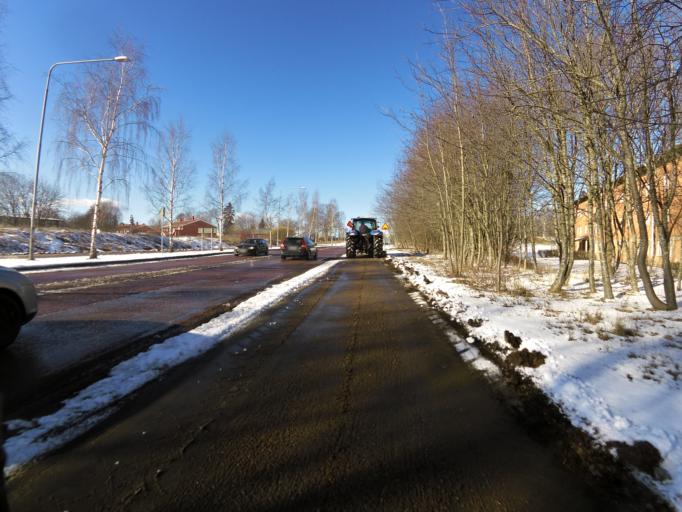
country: SE
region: Gaevleborg
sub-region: Gavle Kommun
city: Gavle
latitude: 60.6710
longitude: 17.1829
